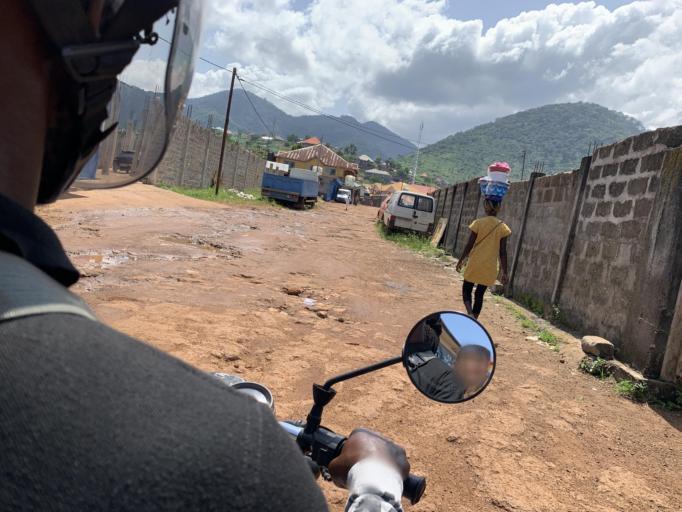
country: SL
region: Western Area
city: Hastings
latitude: 8.3749
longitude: -13.1327
